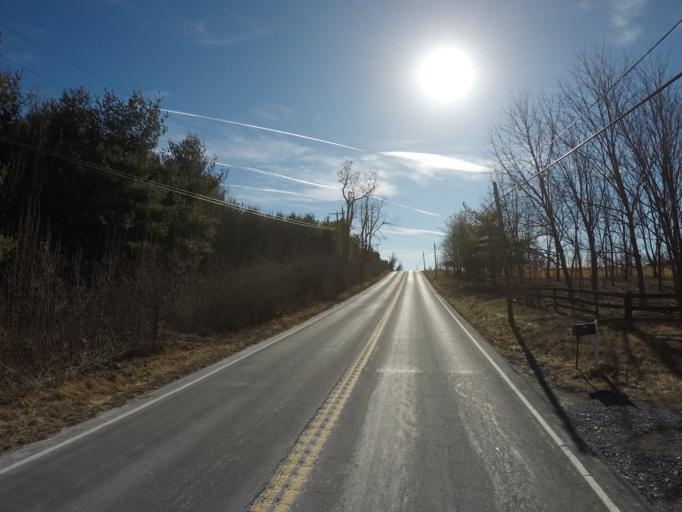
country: US
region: Maryland
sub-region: Frederick County
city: Point of Rocks
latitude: 39.2428
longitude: -77.5313
